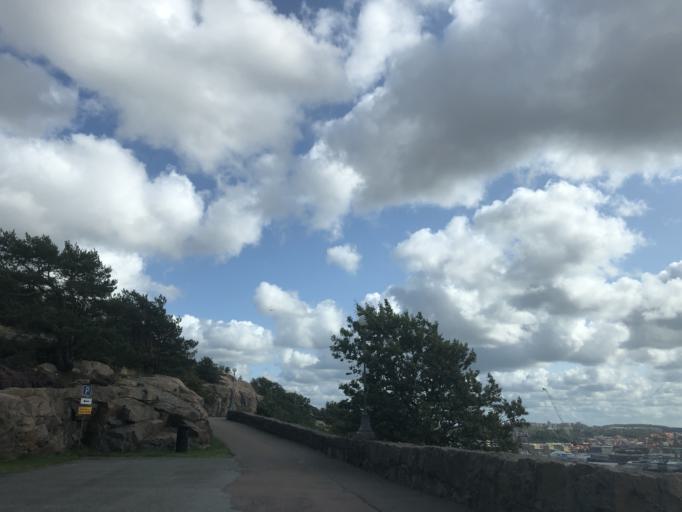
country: SE
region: Vaestra Goetaland
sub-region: Goteborg
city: Majorna
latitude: 57.7142
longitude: 11.9341
